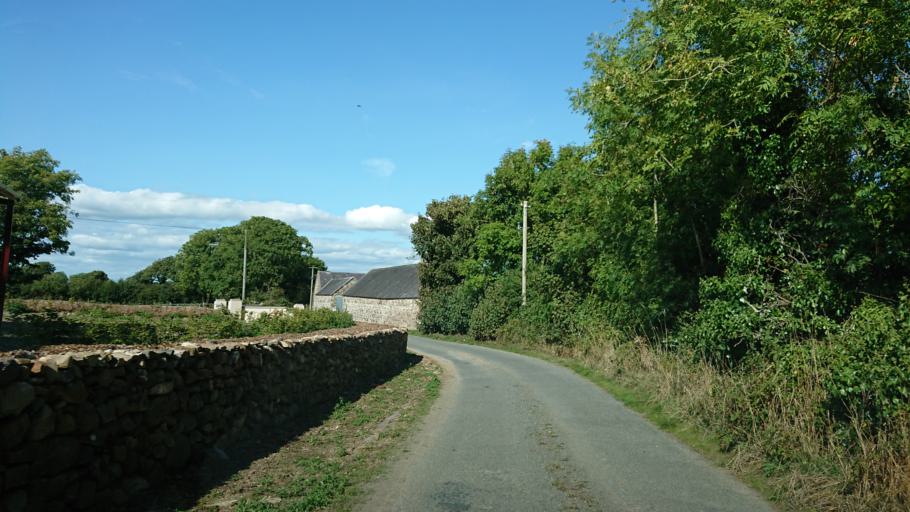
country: IE
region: Munster
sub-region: Waterford
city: Waterford
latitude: 52.2122
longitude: -7.0543
